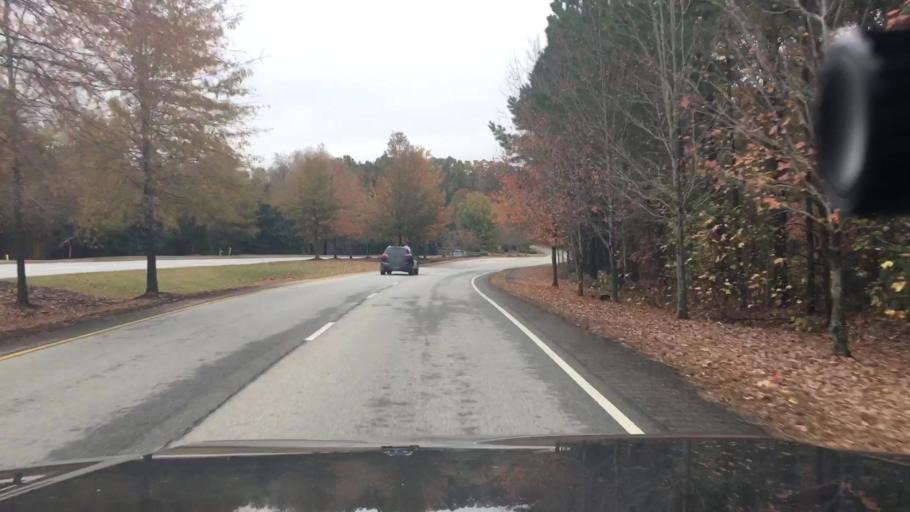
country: US
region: Georgia
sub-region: Coweta County
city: East Newnan
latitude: 33.3893
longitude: -84.7452
